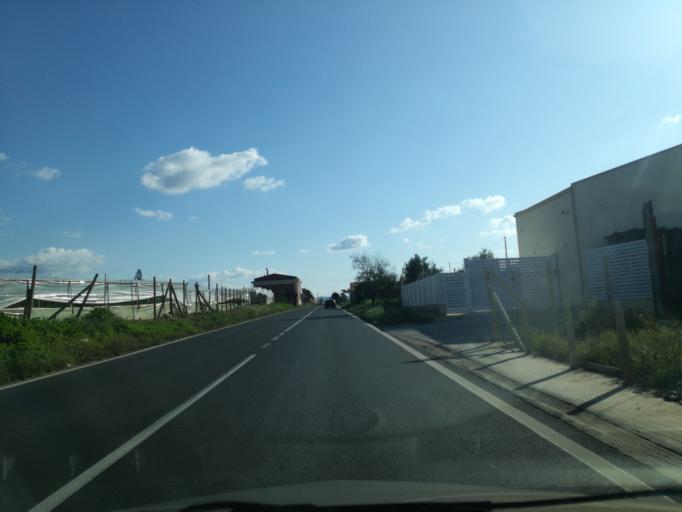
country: IT
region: Sicily
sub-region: Ragusa
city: Acate
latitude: 36.9712
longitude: 14.4760
